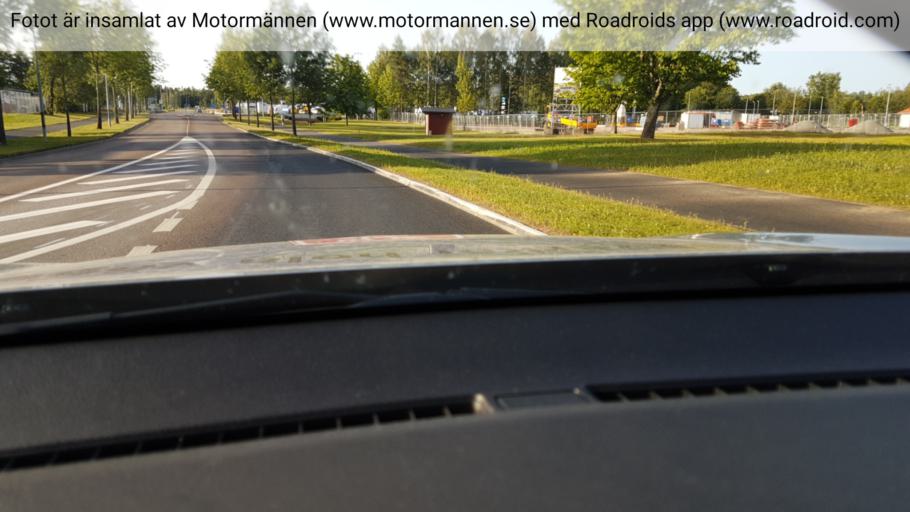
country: SE
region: Joenkoeping
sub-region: Varnamo Kommun
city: Varnamo
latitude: 57.1873
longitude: 14.0628
